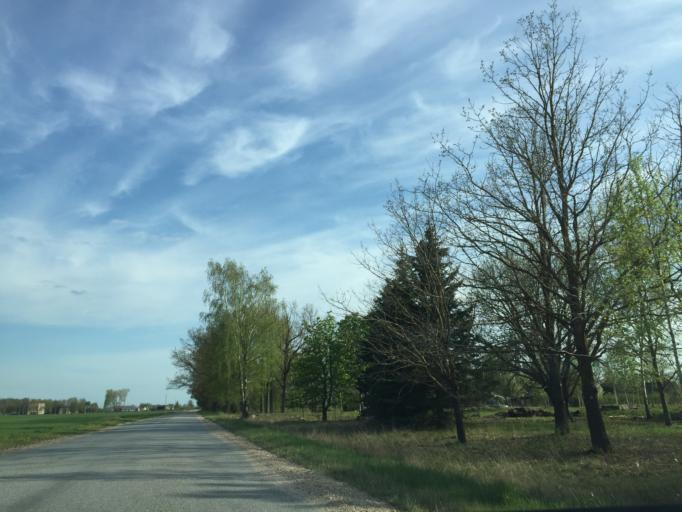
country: LV
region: Bauskas Rajons
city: Bauska
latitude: 56.3709
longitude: 24.2273
